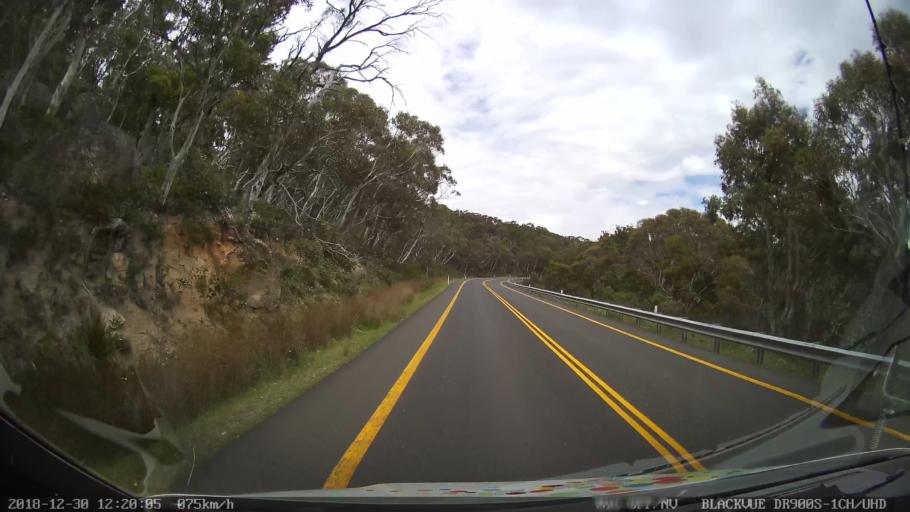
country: AU
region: New South Wales
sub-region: Snowy River
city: Jindabyne
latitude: -36.3458
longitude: 148.5342
